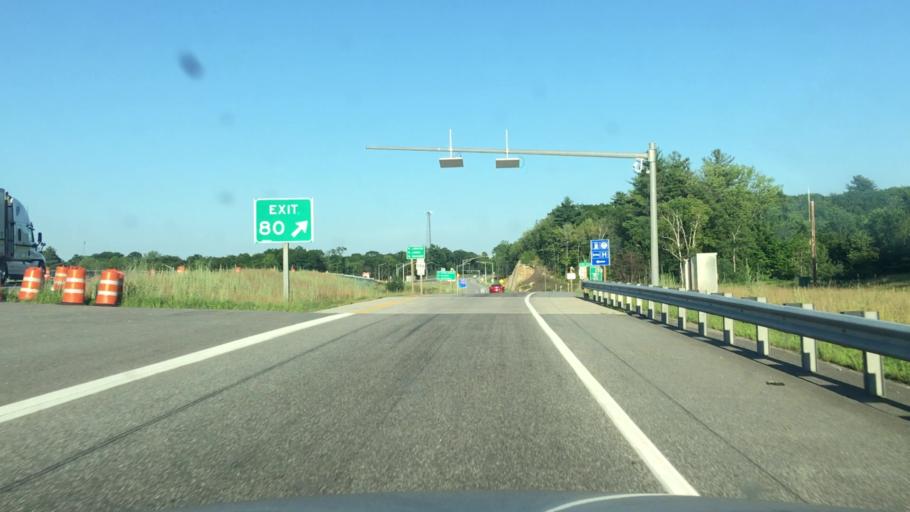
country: US
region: Maine
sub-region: Androscoggin County
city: Lewiston
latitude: 44.0722
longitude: -70.1877
